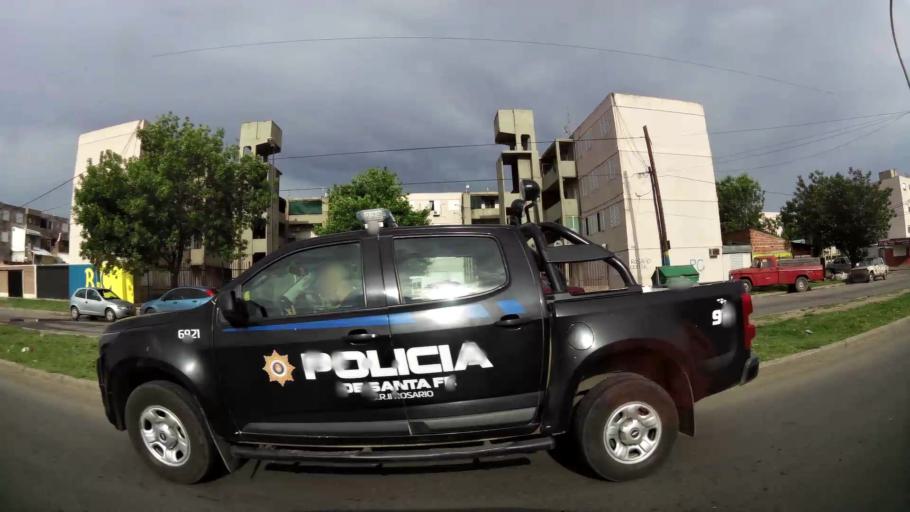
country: AR
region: Santa Fe
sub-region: Departamento de Rosario
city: Rosario
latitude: -32.9847
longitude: -60.6886
